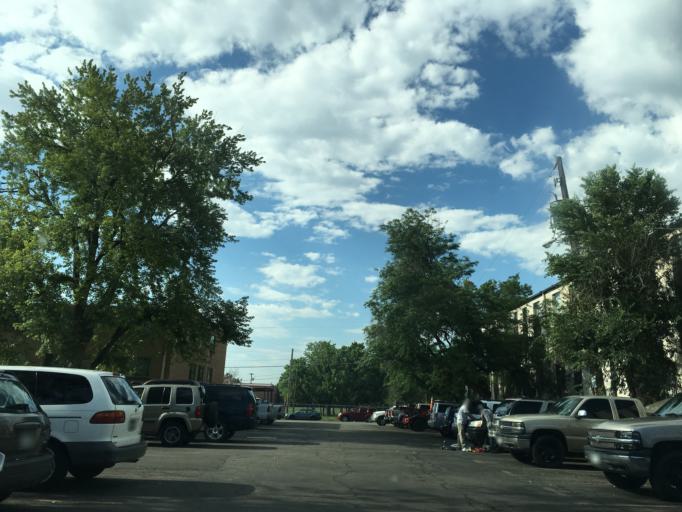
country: US
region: Colorado
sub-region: Arapahoe County
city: Sheridan
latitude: 39.6919
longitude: -105.0273
